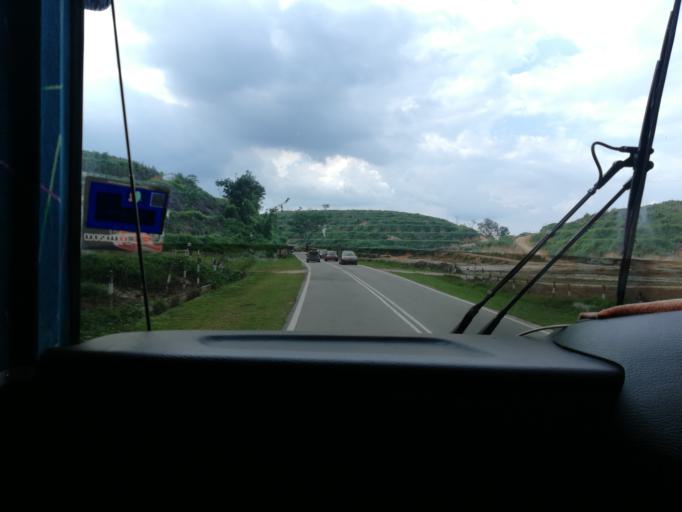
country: MY
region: Kedah
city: Kulim
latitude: 5.3076
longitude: 100.6135
